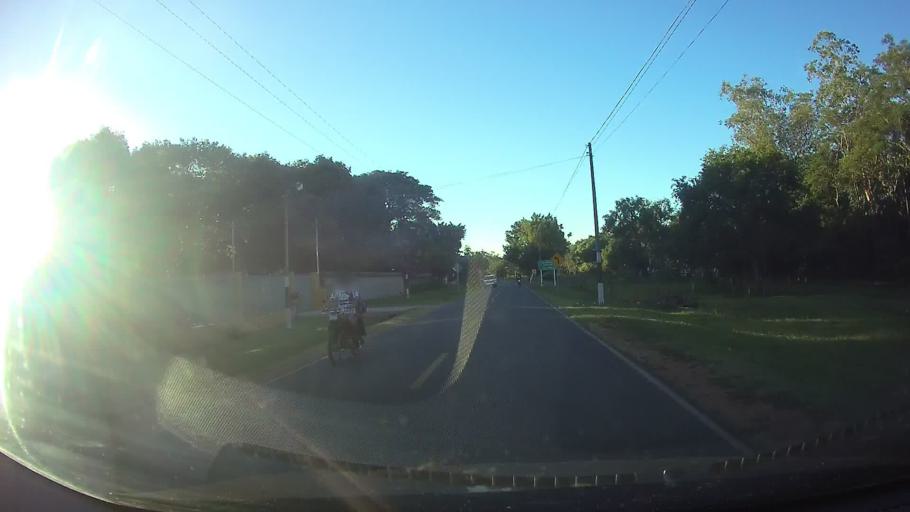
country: PY
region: Central
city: Aregua
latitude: -25.2813
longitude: -57.3993
